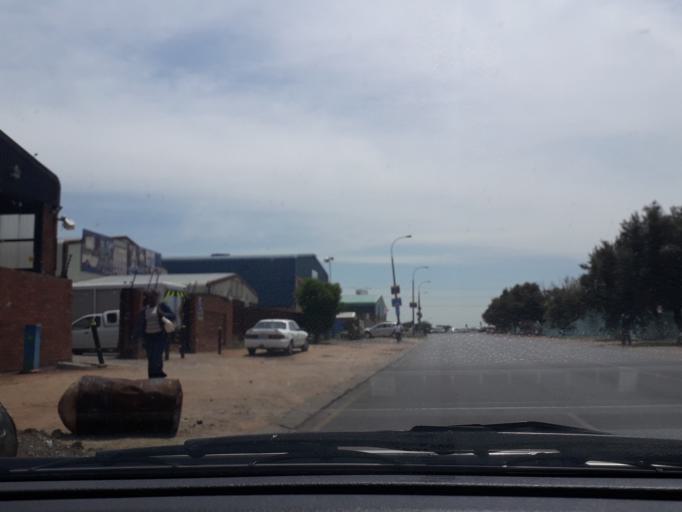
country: ZA
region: Gauteng
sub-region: City of Johannesburg Metropolitan Municipality
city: Roodepoort
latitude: -26.1947
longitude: 27.9221
